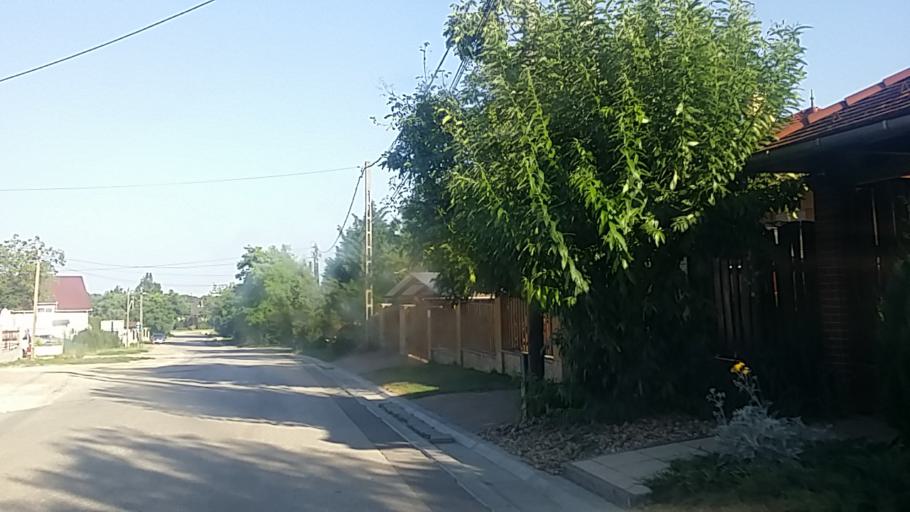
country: HU
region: Pest
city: Urom
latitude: 47.5831
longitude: 19.0248
